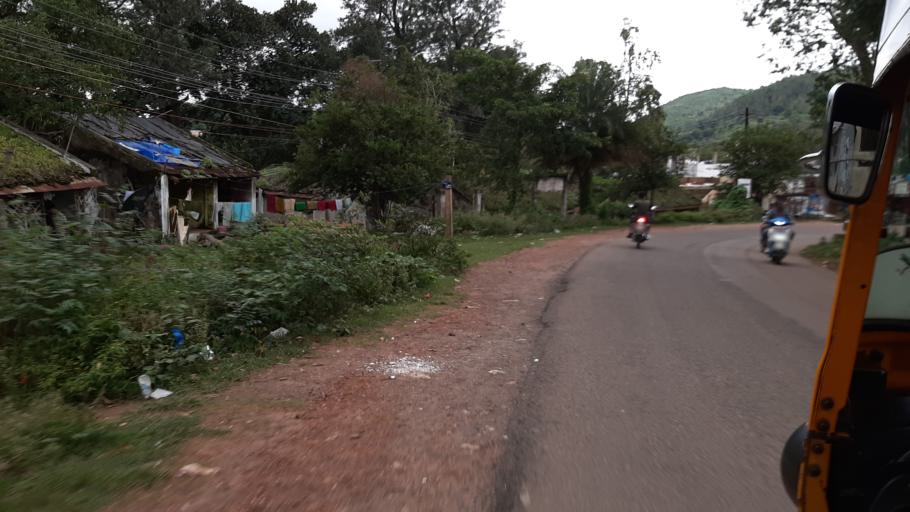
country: IN
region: Andhra Pradesh
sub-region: Vizianagaram District
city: Salur
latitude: 18.2370
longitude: 83.0086
